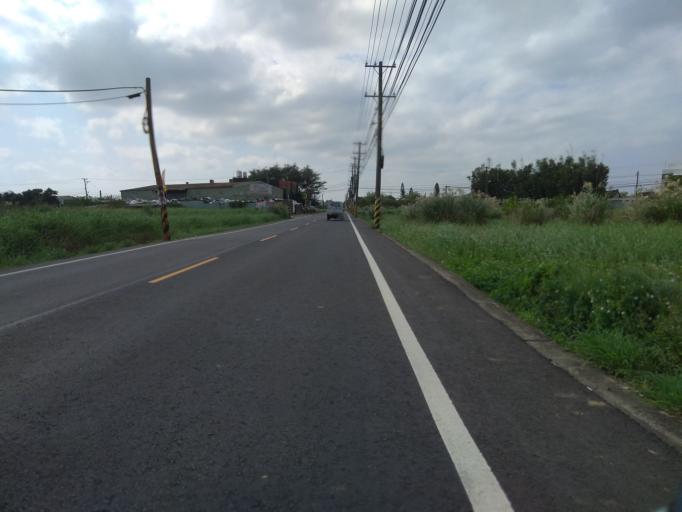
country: TW
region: Taiwan
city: Taoyuan City
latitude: 25.0706
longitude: 121.2465
